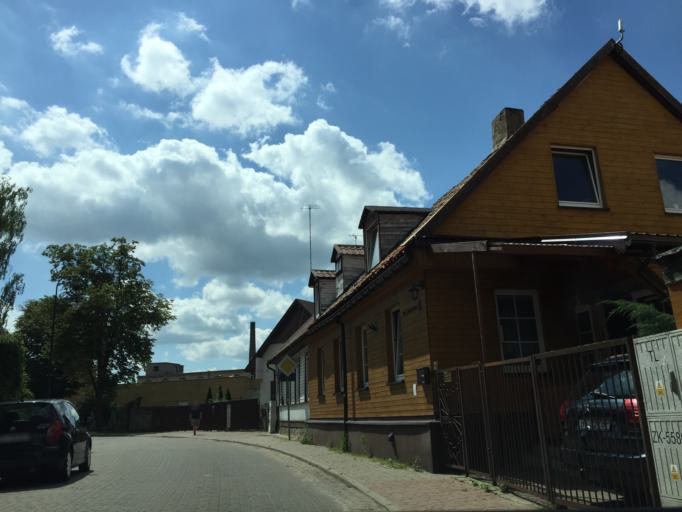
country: PL
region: Podlasie
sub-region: Bialystok
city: Bialystok
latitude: 53.1321
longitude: 23.1762
